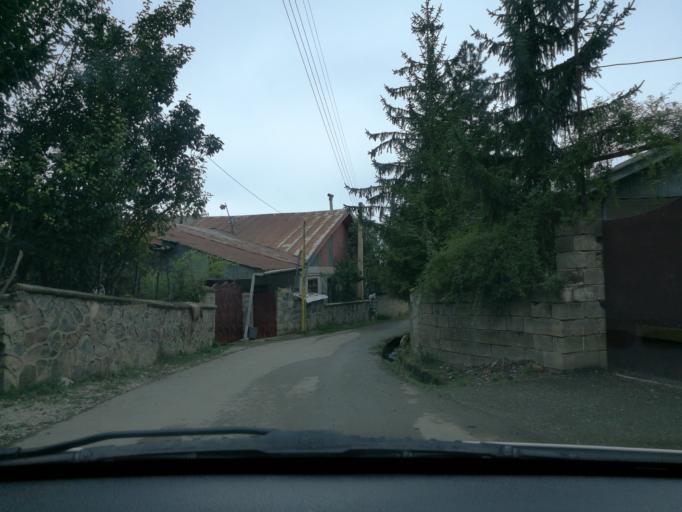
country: IR
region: Mazandaran
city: `Abbasabad
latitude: 36.4942
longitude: 51.2077
